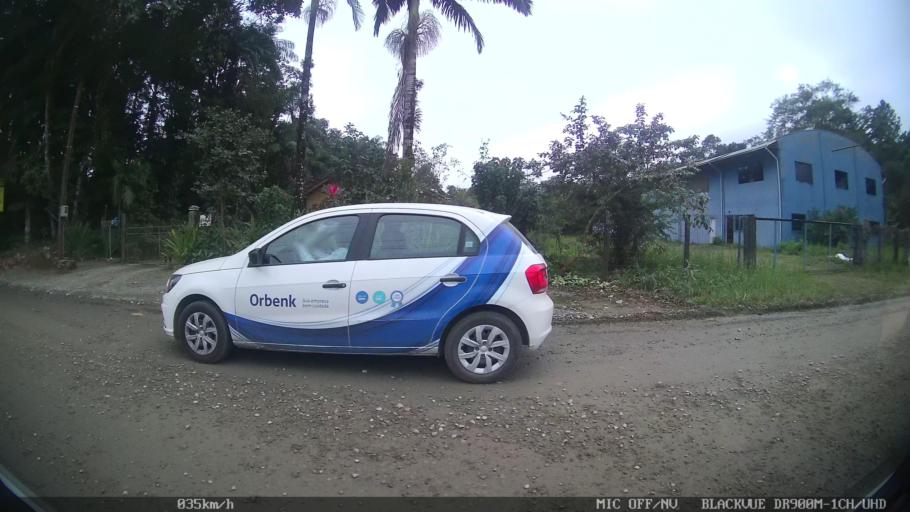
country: BR
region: Santa Catarina
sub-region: Joinville
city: Joinville
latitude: -26.2377
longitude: -48.9263
